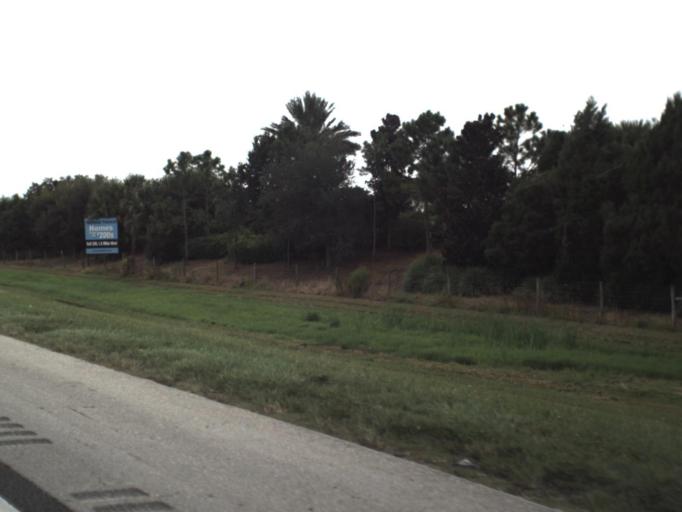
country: US
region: Florida
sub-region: Manatee County
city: Ellenton
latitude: 27.5146
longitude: -82.5023
